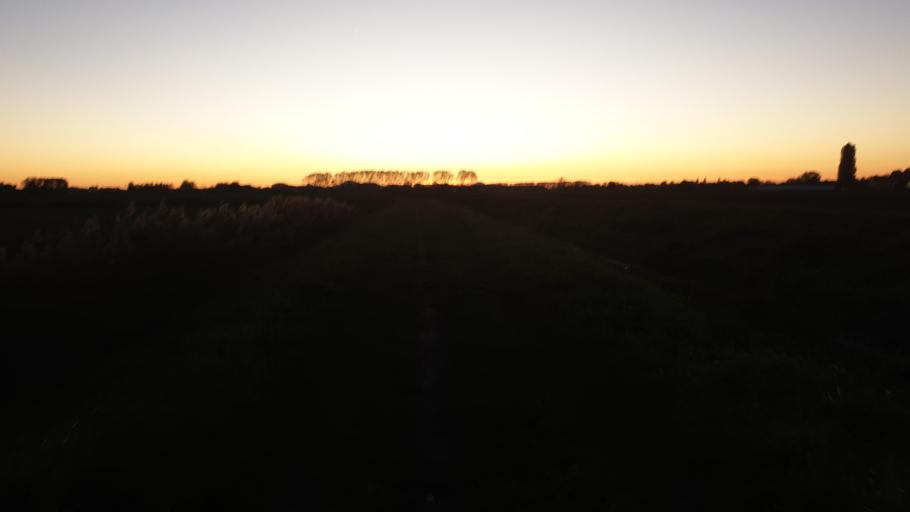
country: IT
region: Veneto
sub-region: Provincia di Venezia
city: Fiesso d'Artico
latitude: 45.4333
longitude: 12.0340
